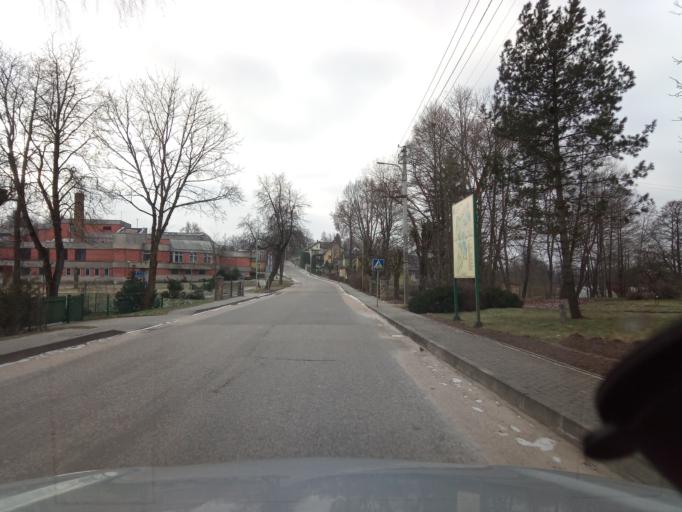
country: LT
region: Alytaus apskritis
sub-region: Alytaus rajonas
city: Daugai
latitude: 54.3650
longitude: 24.3442
